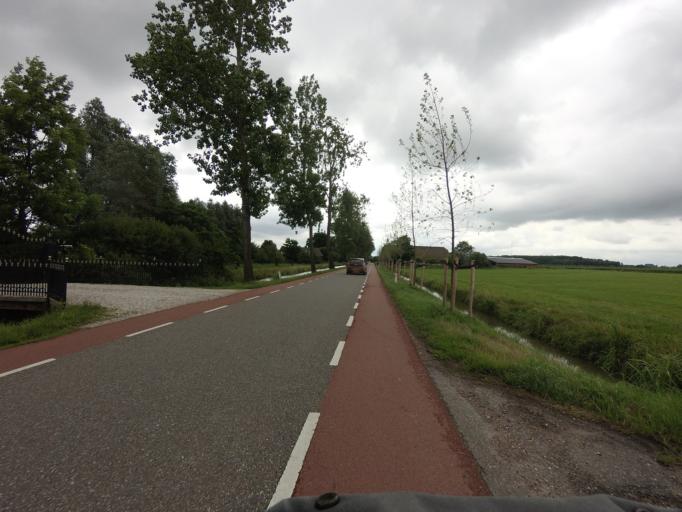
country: NL
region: Utrecht
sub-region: Gemeente IJsselstein
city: IJsselstein
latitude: 52.0513
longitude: 5.0333
